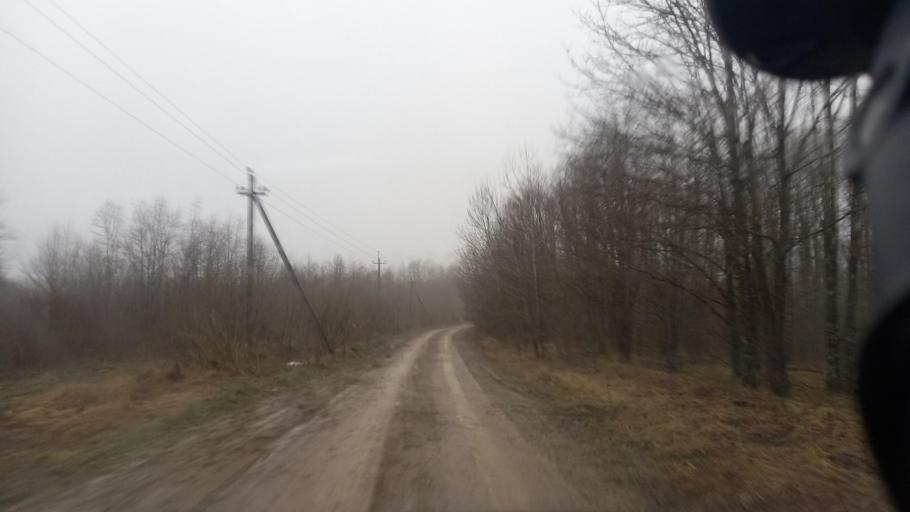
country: RU
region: Krasnodarskiy
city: Saratovskaya
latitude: 44.6143
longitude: 39.2451
